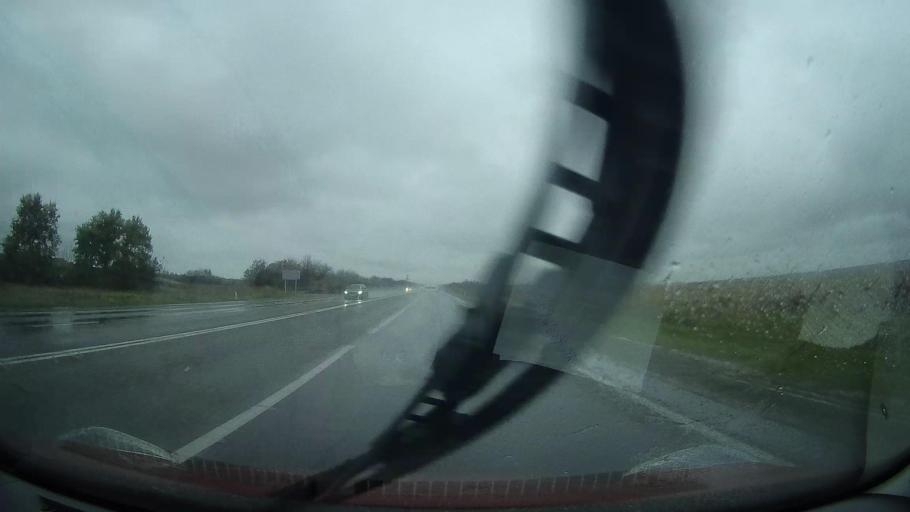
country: RU
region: Stavropol'skiy
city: Nevinnomyssk
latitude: 44.6320
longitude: 42.0202
